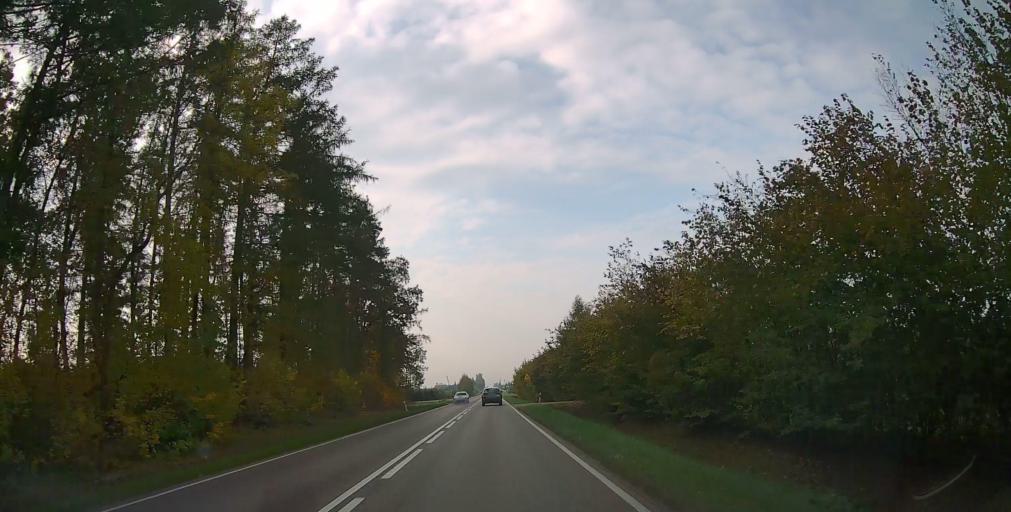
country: PL
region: Masovian Voivodeship
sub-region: Powiat grojecki
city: Belsk Duzy
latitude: 51.7910
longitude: 20.7829
